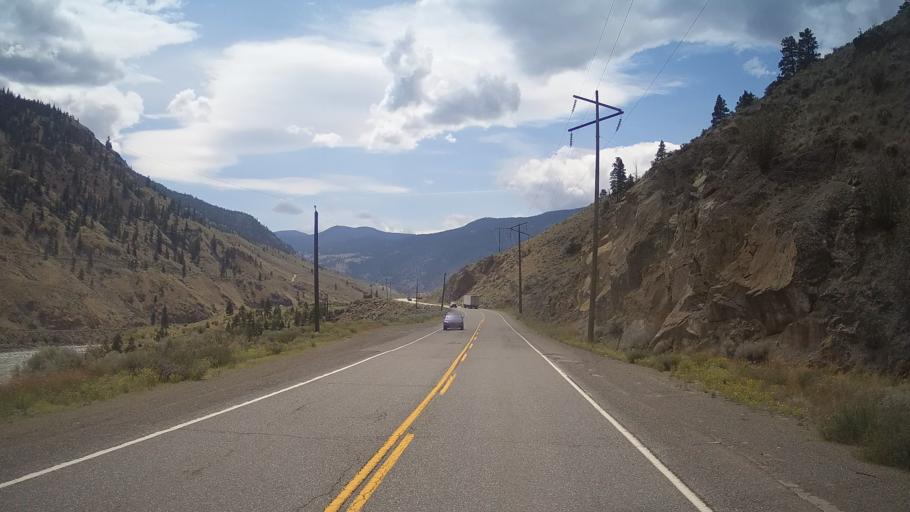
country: CA
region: British Columbia
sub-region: Thompson-Nicola Regional District
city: Ashcroft
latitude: 50.4651
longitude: -121.3008
